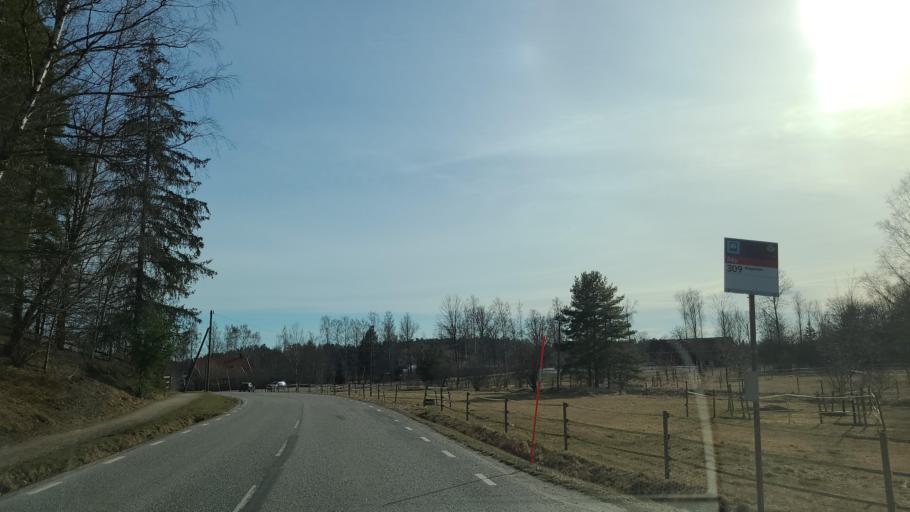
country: SE
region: Stockholm
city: Stenhamra
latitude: 59.2830
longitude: 17.7154
